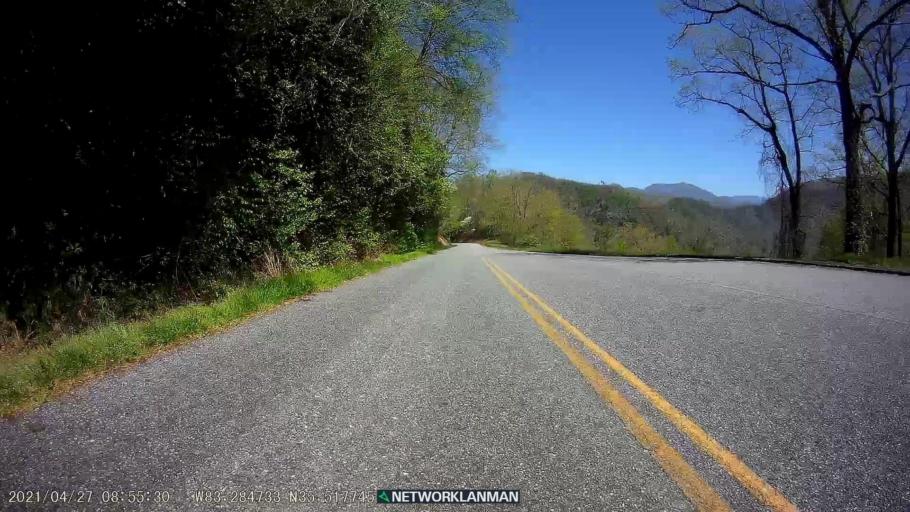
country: US
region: North Carolina
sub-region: Swain County
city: Cherokee
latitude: 35.5174
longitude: -83.2848
